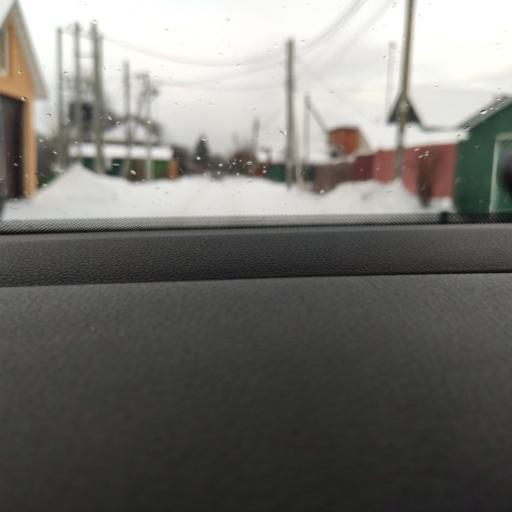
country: RU
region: Moskovskaya
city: Ramenskoye
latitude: 55.4774
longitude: 38.1532
